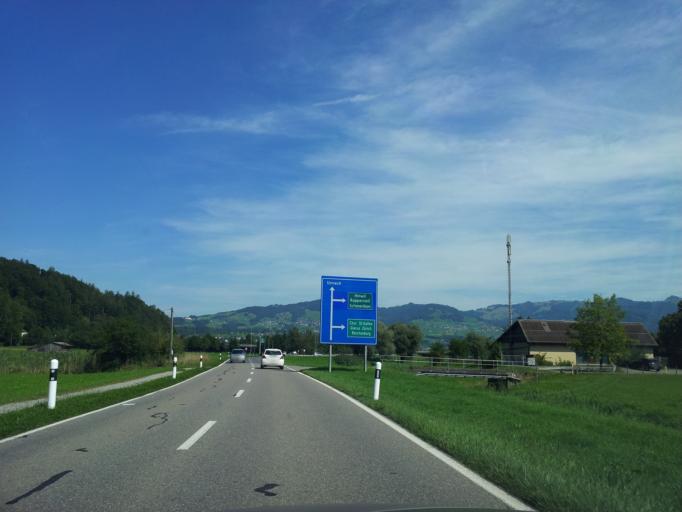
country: CH
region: Schwyz
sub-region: Bezirk March
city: Tuggen
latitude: 47.2079
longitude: 8.9575
